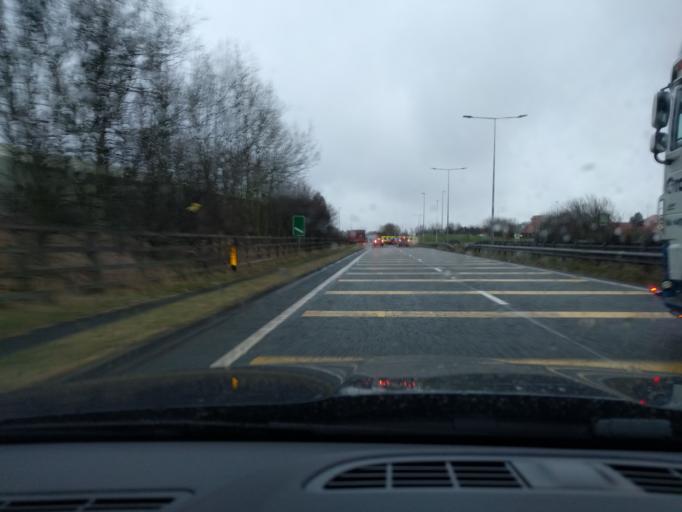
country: GB
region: England
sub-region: Northumberland
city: Berwick-Upon-Tweed
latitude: 55.7872
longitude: -2.0183
